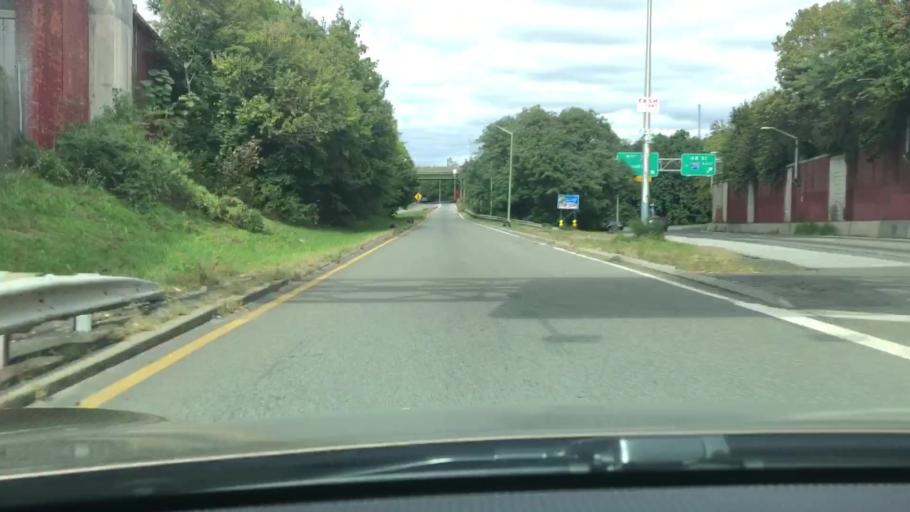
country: US
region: New York
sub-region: Queens County
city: Long Island City
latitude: 40.7331
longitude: -73.9202
